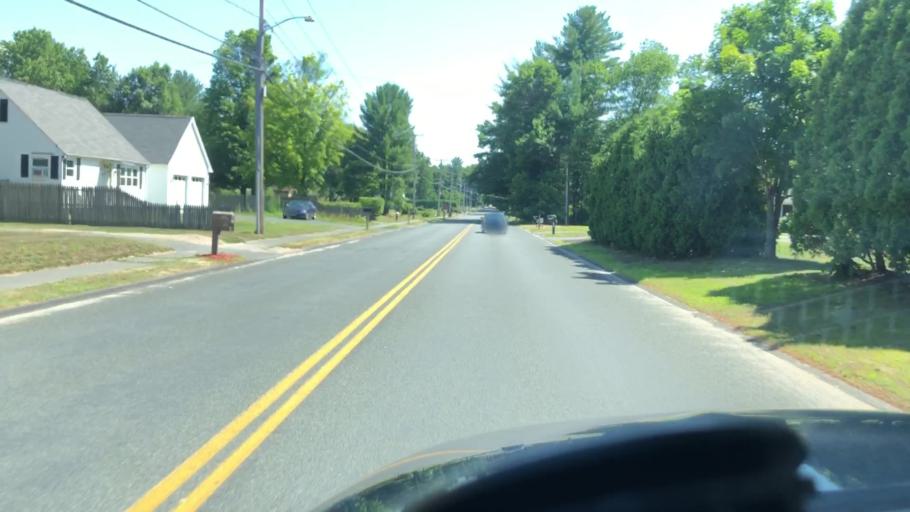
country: US
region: Massachusetts
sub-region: Hampshire County
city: Easthampton
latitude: 42.2300
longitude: -72.6861
